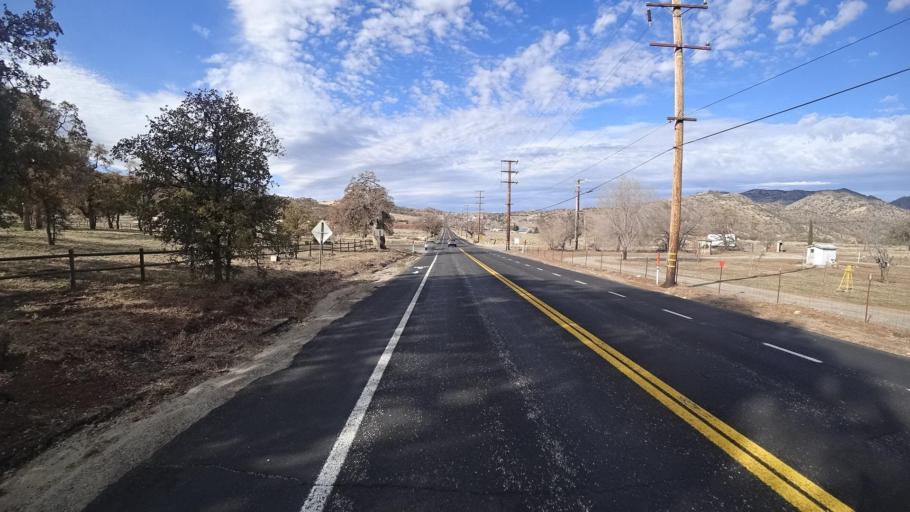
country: US
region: California
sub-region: Kern County
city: Golden Hills
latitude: 35.1106
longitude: -118.5055
